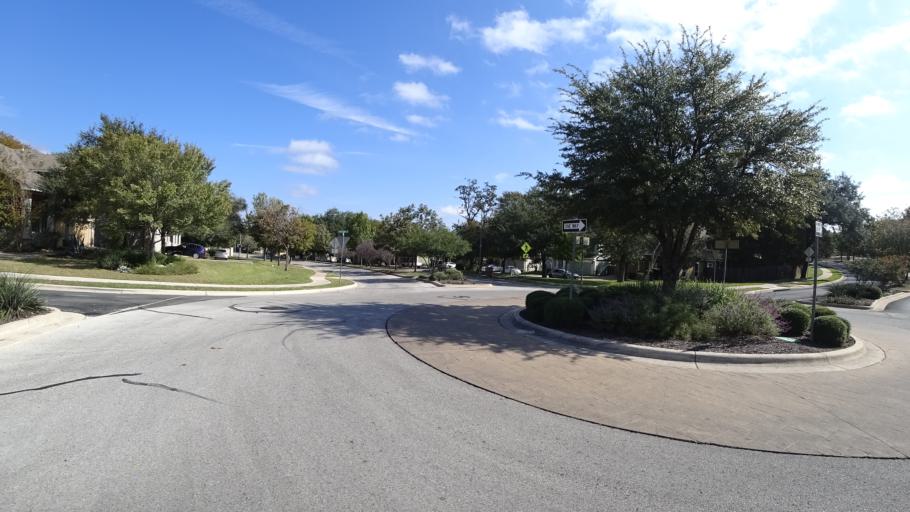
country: US
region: Texas
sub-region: Travis County
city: Shady Hollow
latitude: 30.1887
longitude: -97.8185
